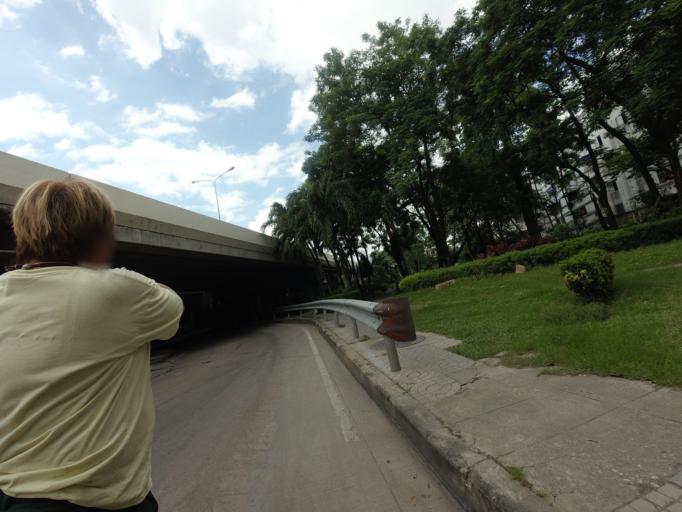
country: TH
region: Bangkok
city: Bang Kapi
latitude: 13.7699
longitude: 100.6567
